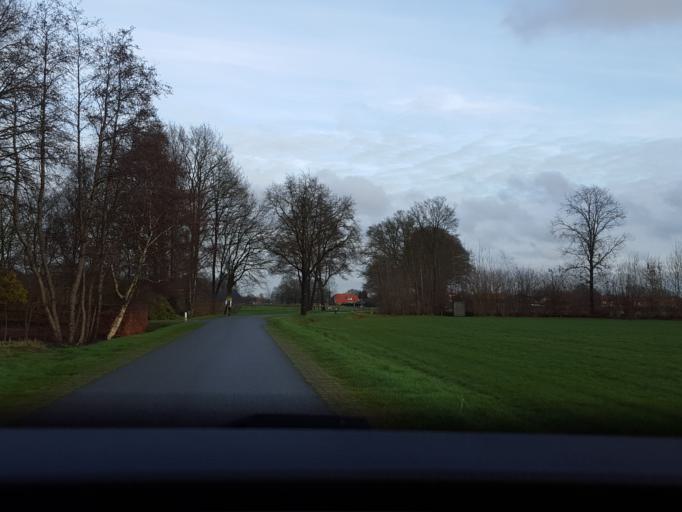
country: NL
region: Gelderland
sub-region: Oude IJsselstreek
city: Varsseveld
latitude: 52.0126
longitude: 6.4599
